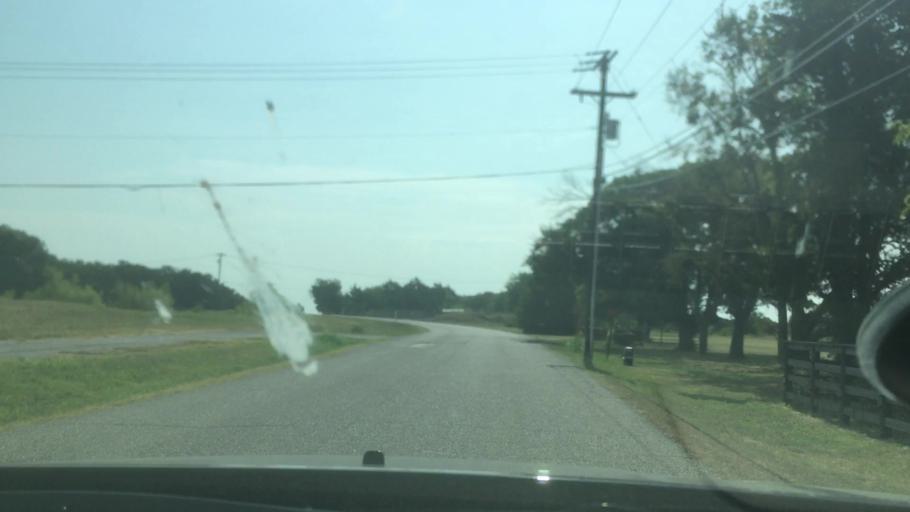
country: US
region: Texas
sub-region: Grayson County
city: Pottsboro
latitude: 33.8150
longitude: -96.7054
